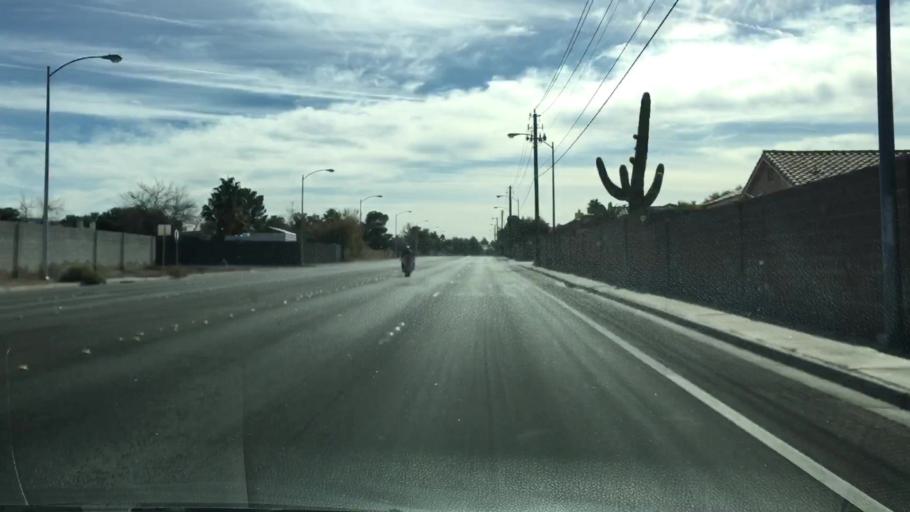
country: US
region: Nevada
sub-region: Clark County
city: Whitney
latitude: 36.0467
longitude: -115.1274
